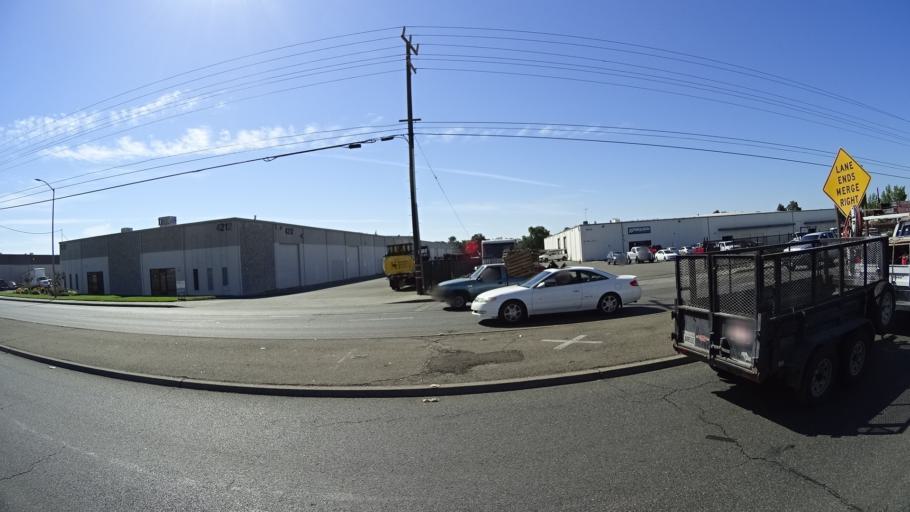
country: US
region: California
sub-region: Sacramento County
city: Arden-Arcade
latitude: 38.6428
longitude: -121.4004
